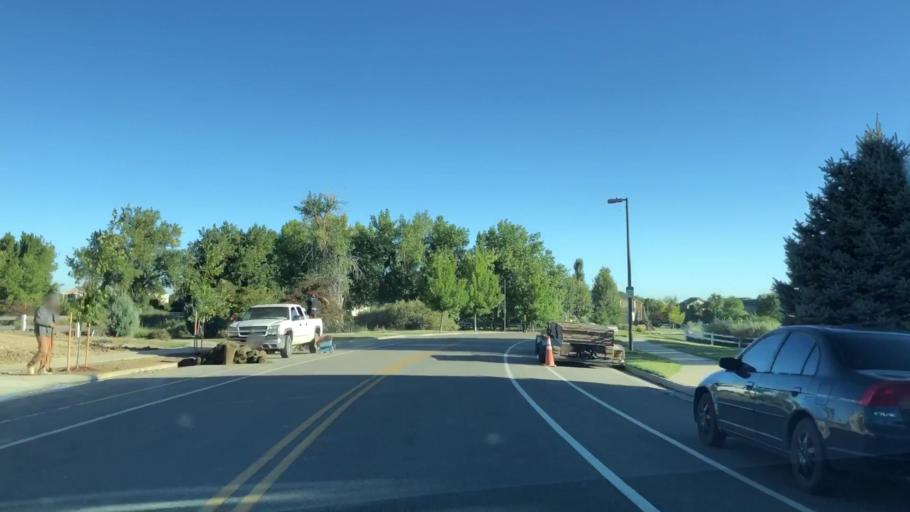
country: US
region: Colorado
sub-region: Larimer County
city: Loveland
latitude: 40.4559
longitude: -105.0322
